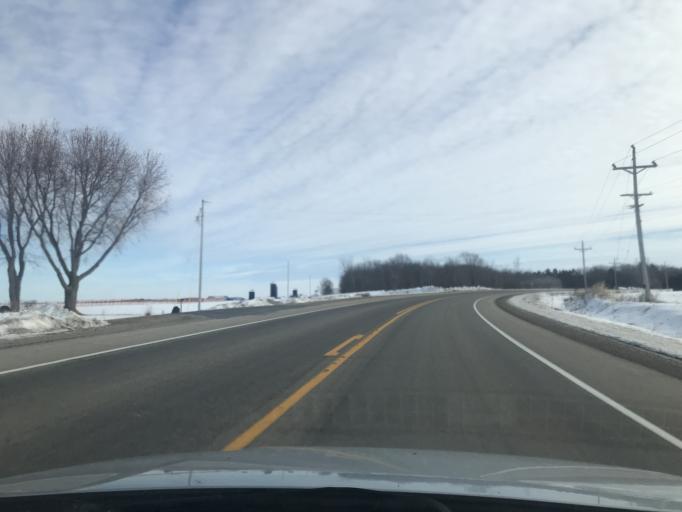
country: US
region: Wisconsin
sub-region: Oconto County
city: Oconto Falls
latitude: 44.8943
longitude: -88.1744
